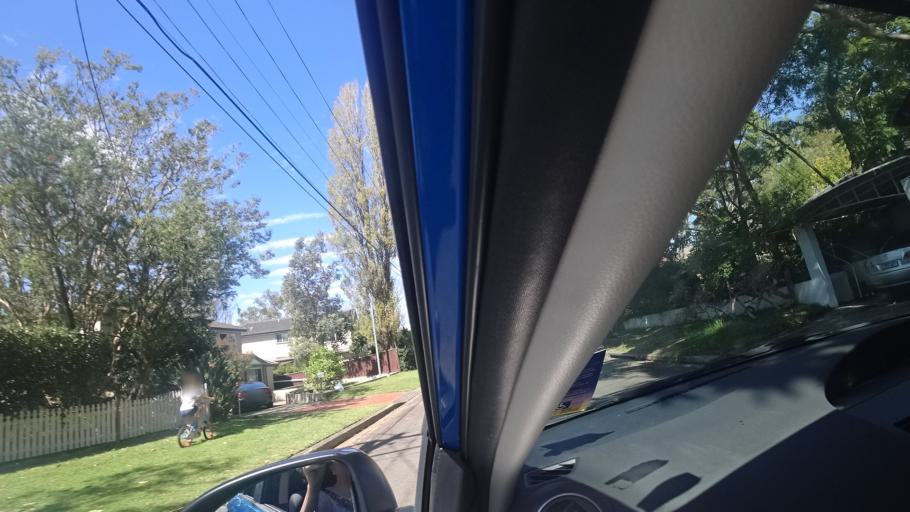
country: AU
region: New South Wales
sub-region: Warringah
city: Allambie Heights
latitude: -33.7616
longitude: 151.2489
